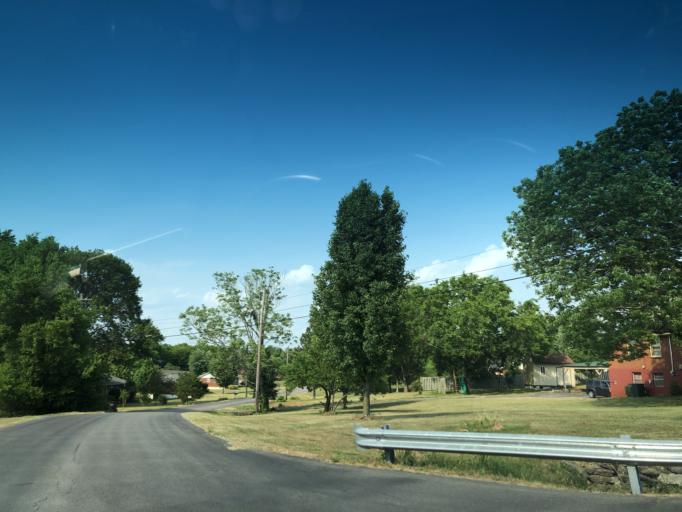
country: US
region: Tennessee
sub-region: Davidson County
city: Goodlettsville
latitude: 36.2784
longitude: -86.7230
